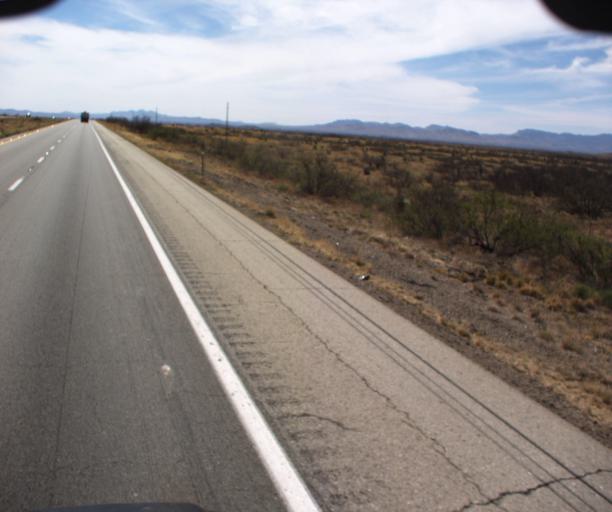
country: US
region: Arizona
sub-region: Cochise County
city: Willcox
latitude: 32.3357
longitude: -109.7619
